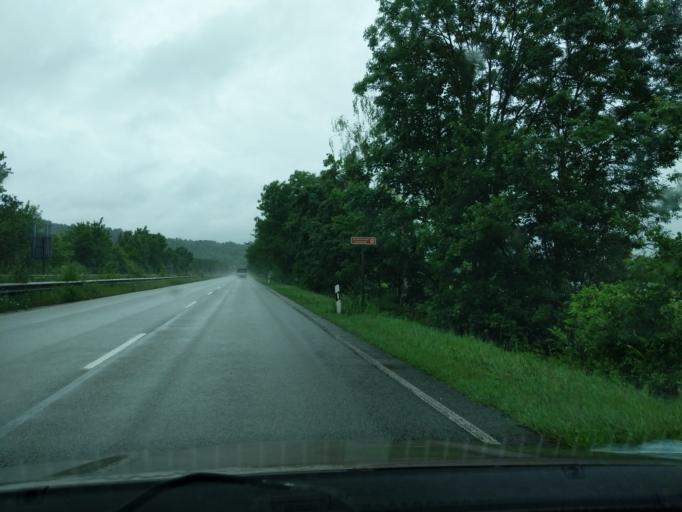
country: DE
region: Bavaria
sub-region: Upper Palatinate
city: Sinzing
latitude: 49.0275
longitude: 12.0456
